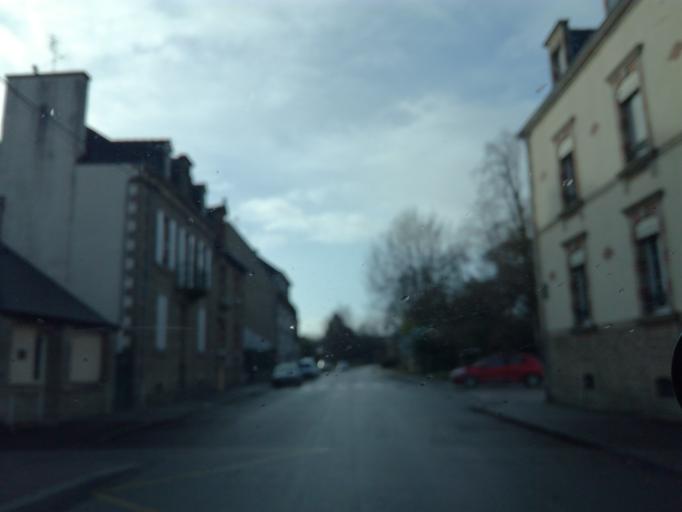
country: FR
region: Brittany
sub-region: Departement du Morbihan
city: Pontivy
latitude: 48.0603
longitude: -2.9677
